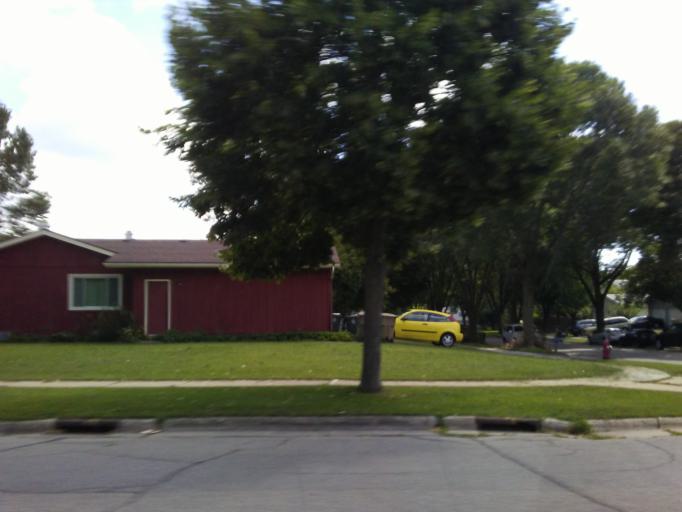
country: US
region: Wisconsin
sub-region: Dane County
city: Verona
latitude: 43.0300
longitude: -89.4970
